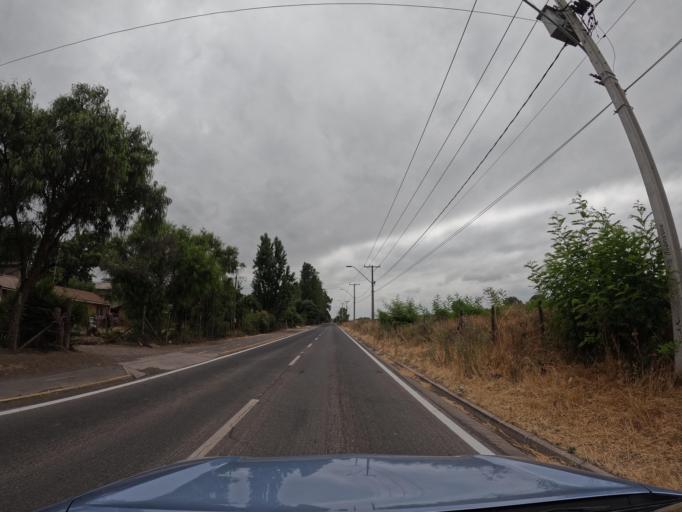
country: CL
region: O'Higgins
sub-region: Provincia de Colchagua
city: Chimbarongo
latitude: -34.7329
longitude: -71.0618
